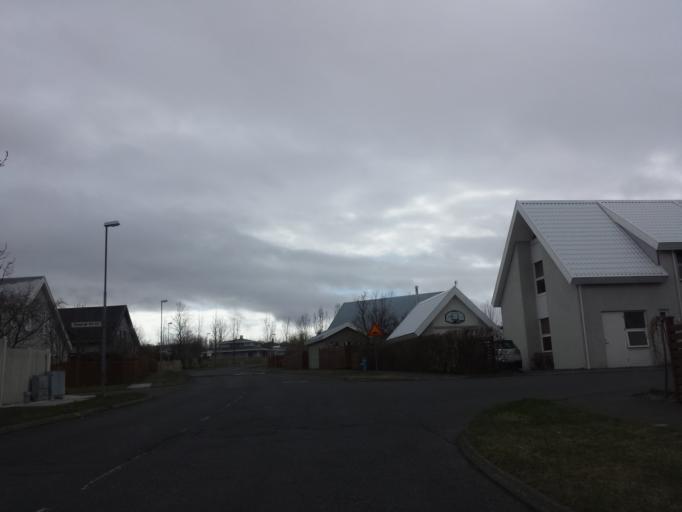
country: IS
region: Capital Region
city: Kopavogur
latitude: 64.0917
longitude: -21.8948
